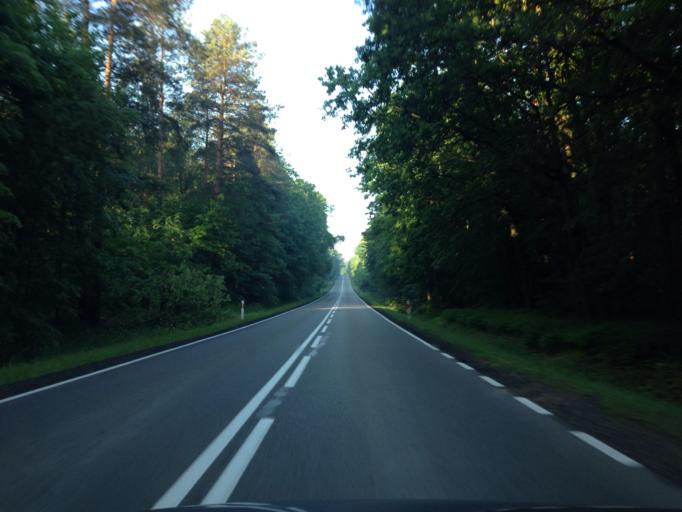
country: PL
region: Pomeranian Voivodeship
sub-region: Powiat kwidzynski
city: Gardeja
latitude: 53.5899
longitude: 18.9107
